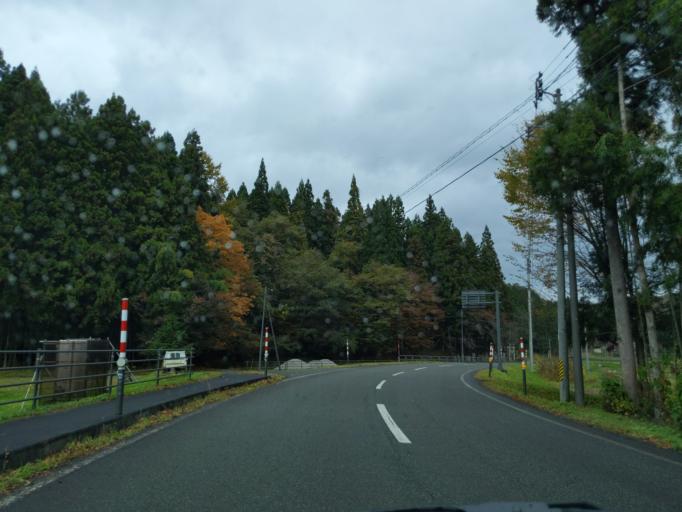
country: JP
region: Iwate
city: Ichinoseki
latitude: 38.9763
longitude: 140.9487
